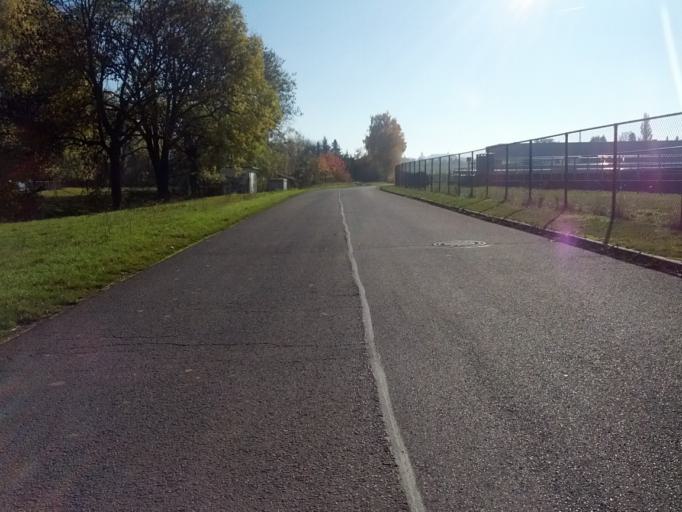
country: DE
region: Thuringia
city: Gotha
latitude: 50.9667
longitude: 10.6994
